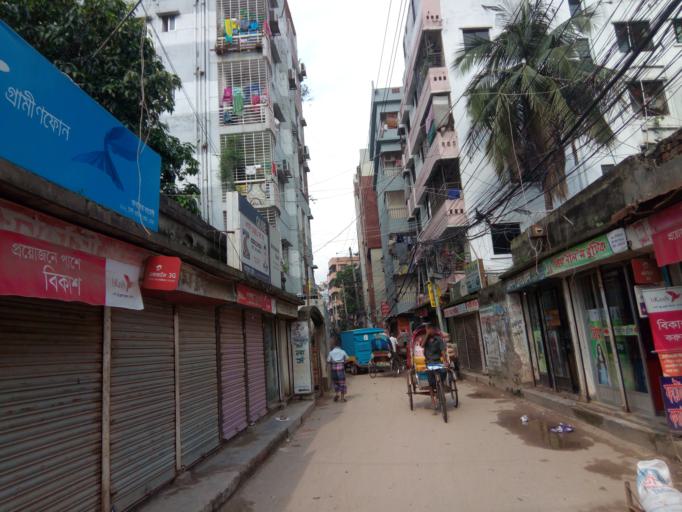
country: BD
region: Dhaka
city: Azimpur
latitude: 23.7410
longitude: 90.3652
